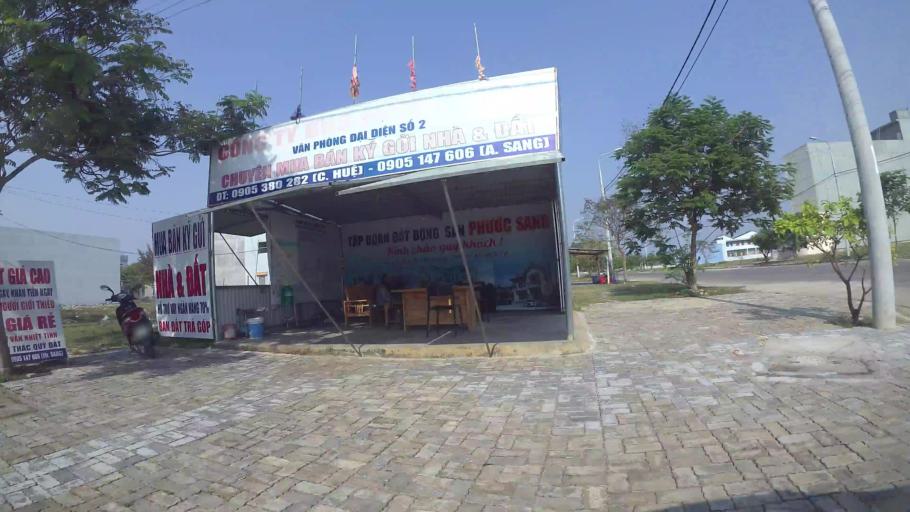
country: VN
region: Da Nang
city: Ngu Hanh Son
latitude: 15.9528
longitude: 108.2597
